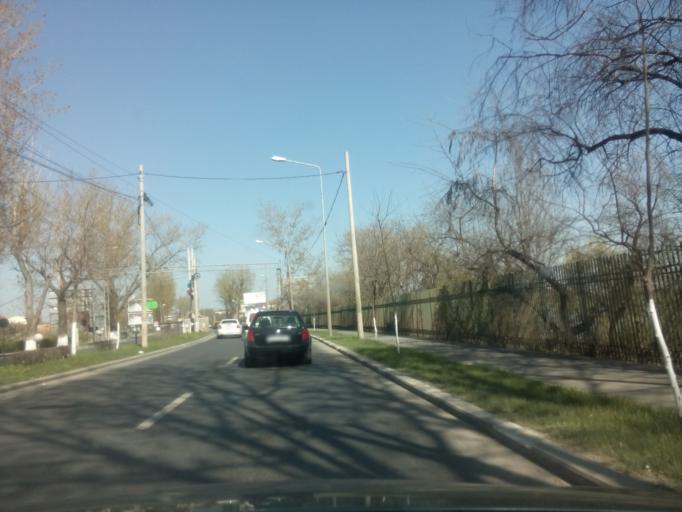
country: RO
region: Ilfov
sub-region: Comuna Pantelimon
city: Pantelimon
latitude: 44.4418
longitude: 26.1964
